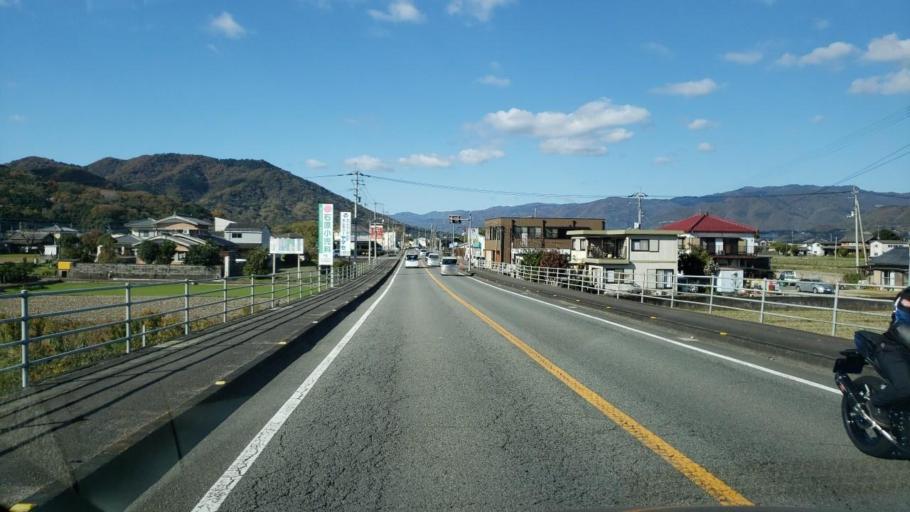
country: JP
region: Tokushima
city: Wakimachi
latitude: 34.0578
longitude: 134.2254
